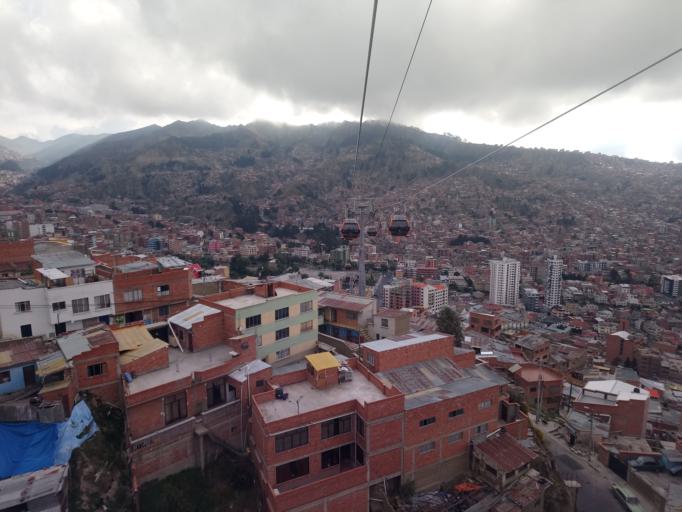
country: BO
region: La Paz
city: La Paz
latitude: -16.4857
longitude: -68.1271
